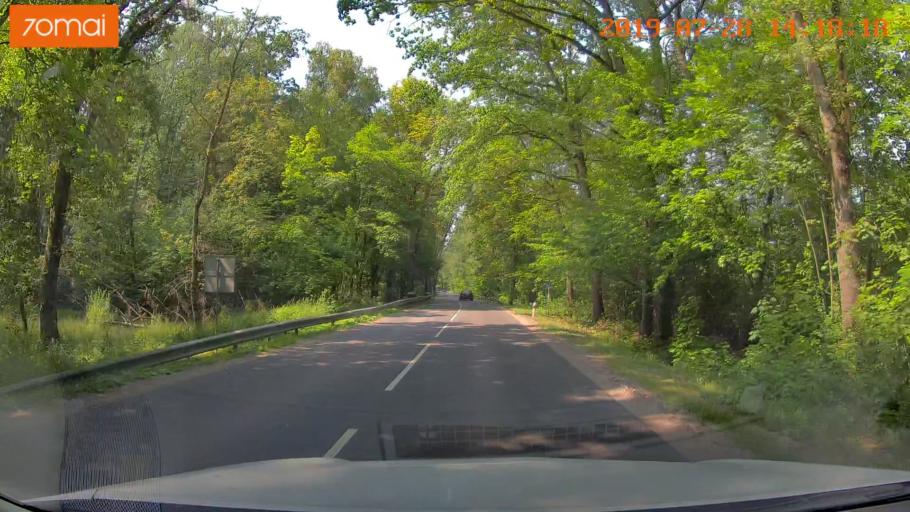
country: RU
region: Kaliningrad
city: Volochayevskoye
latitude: 54.8168
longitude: 20.2424
